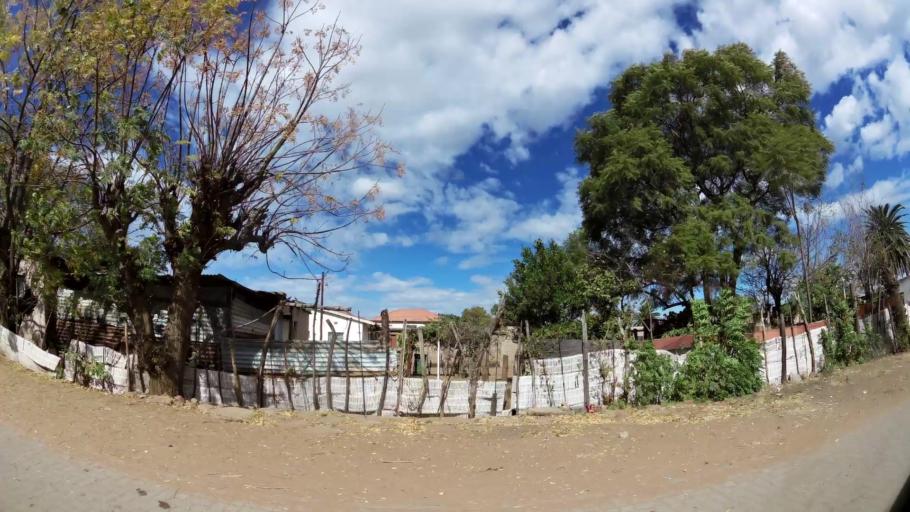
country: ZA
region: Limpopo
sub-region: Waterberg District Municipality
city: Bela-Bela
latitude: -24.8881
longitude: 28.3117
